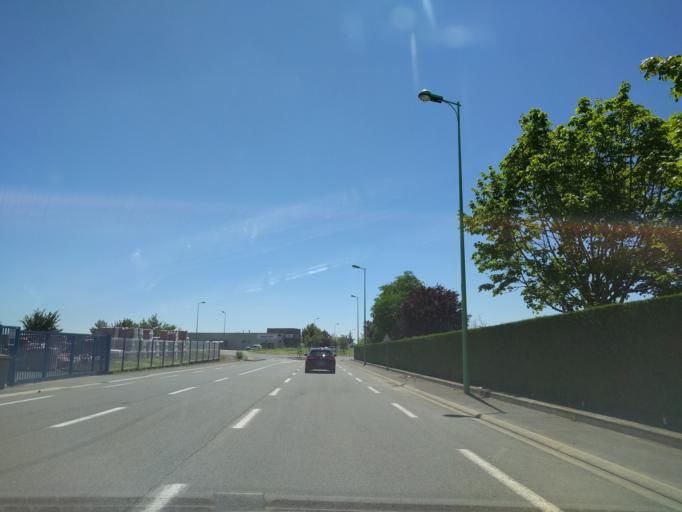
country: FR
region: Poitou-Charentes
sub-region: Departement des Deux-Sevres
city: Aiffres
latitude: 46.3314
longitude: -0.4087
